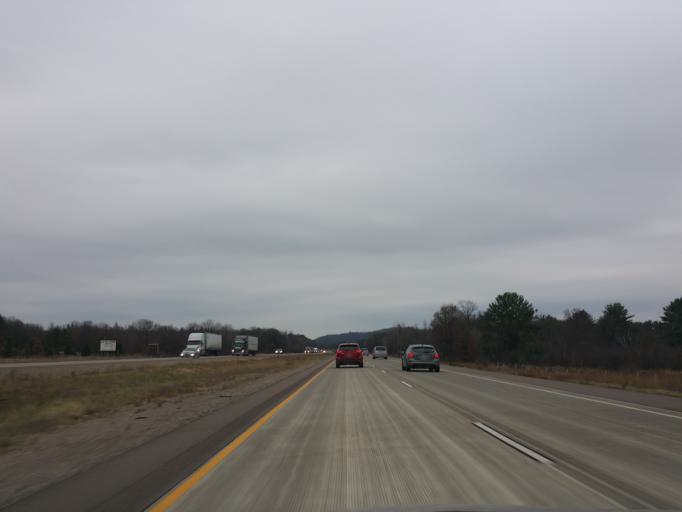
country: US
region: Wisconsin
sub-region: Jackson County
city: Black River Falls
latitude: 44.3615
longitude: -90.9634
